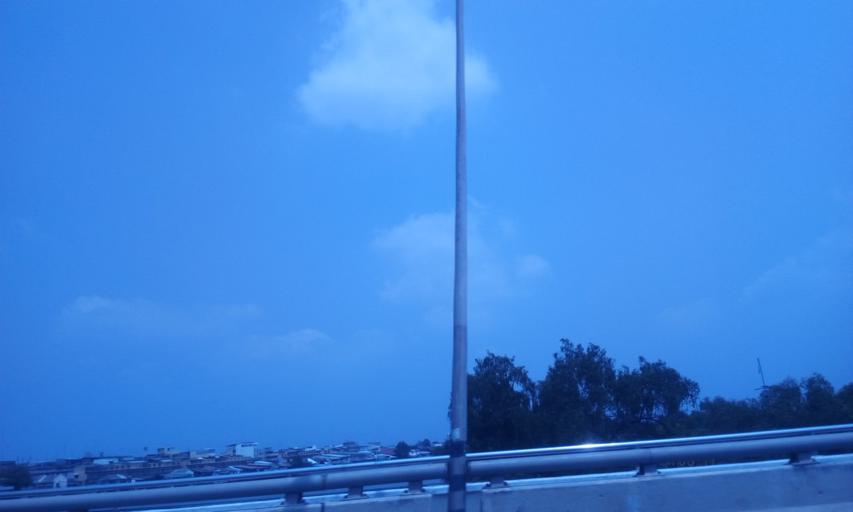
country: TH
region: Chachoengsao
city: Chachoengsao
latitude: 13.6876
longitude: 101.0774
